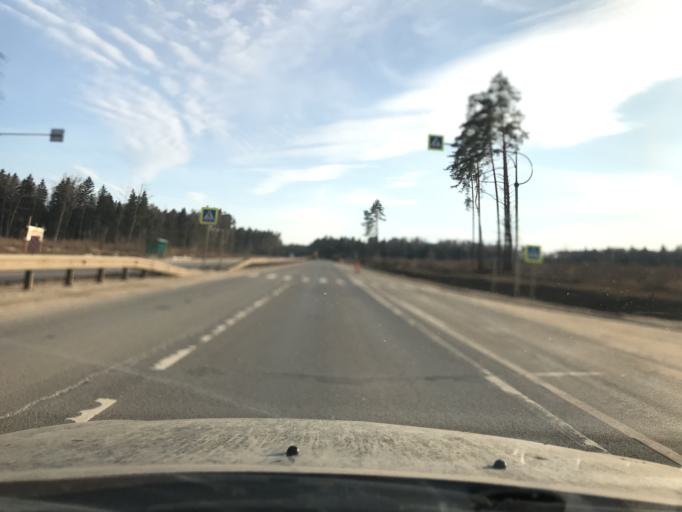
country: RU
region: Kaluga
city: Kaluga
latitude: 54.4199
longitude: 36.2026
